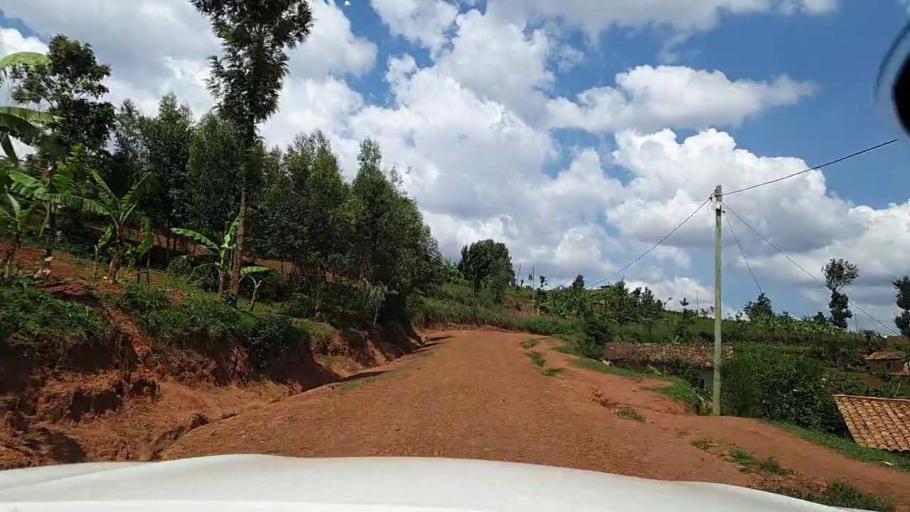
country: RW
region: Southern Province
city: Butare
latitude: -2.7478
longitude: 29.7041
